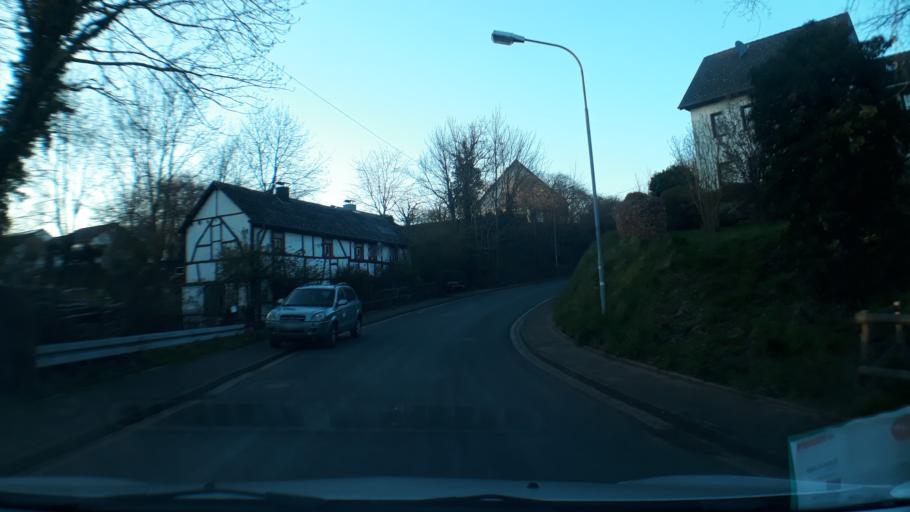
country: DE
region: North Rhine-Westphalia
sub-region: Regierungsbezirk Koln
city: Mechernich
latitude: 50.6047
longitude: 6.5957
